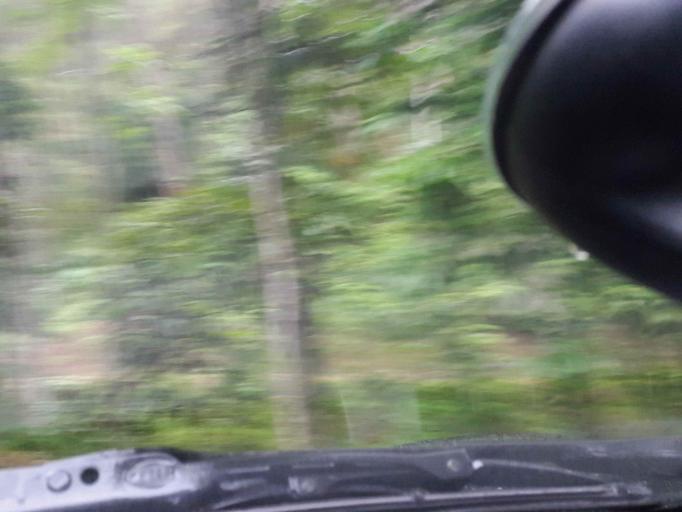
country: ID
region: Central Java
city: Kutoarjo
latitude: -7.5430
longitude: 109.9917
